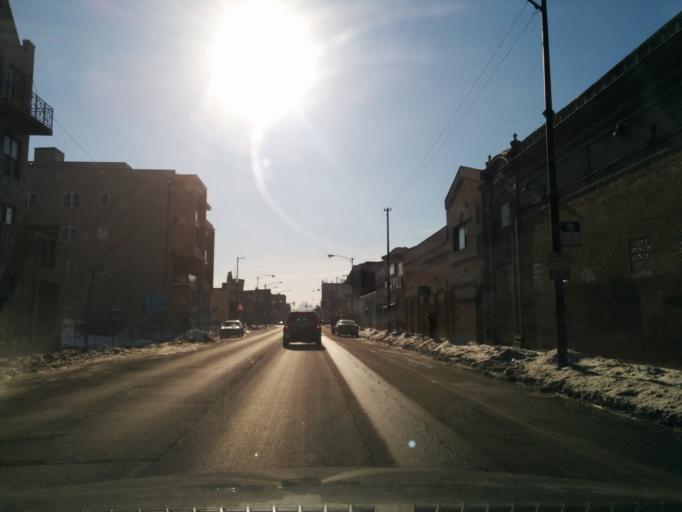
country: US
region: Illinois
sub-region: Cook County
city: Lincolnwood
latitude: 41.9270
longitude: -87.7041
